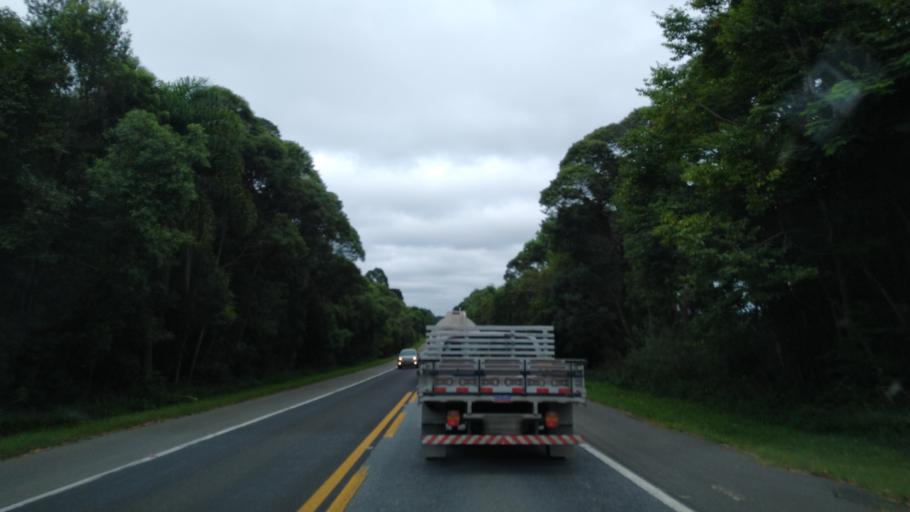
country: BR
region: Santa Catarina
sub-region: Tres Barras
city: Tres Barras
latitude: -26.1720
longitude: -50.0828
